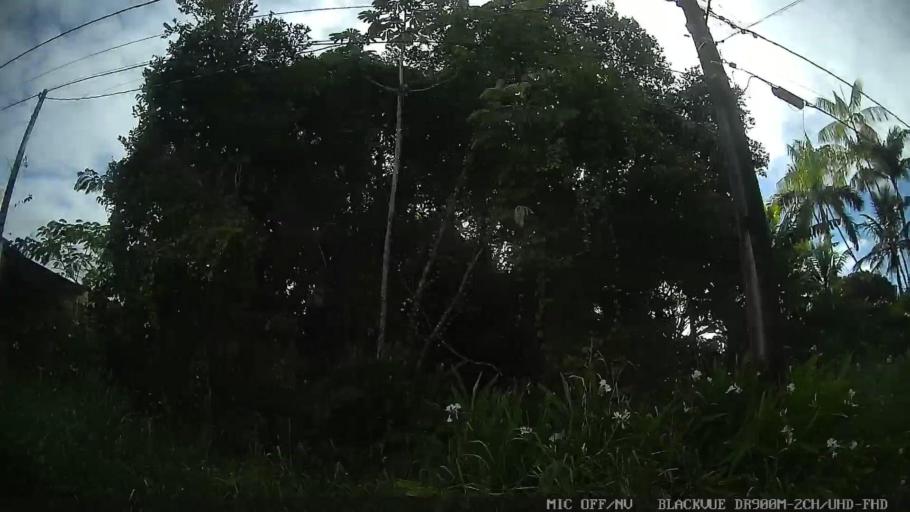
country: BR
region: Sao Paulo
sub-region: Peruibe
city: Peruibe
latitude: -24.2325
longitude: -46.9138
